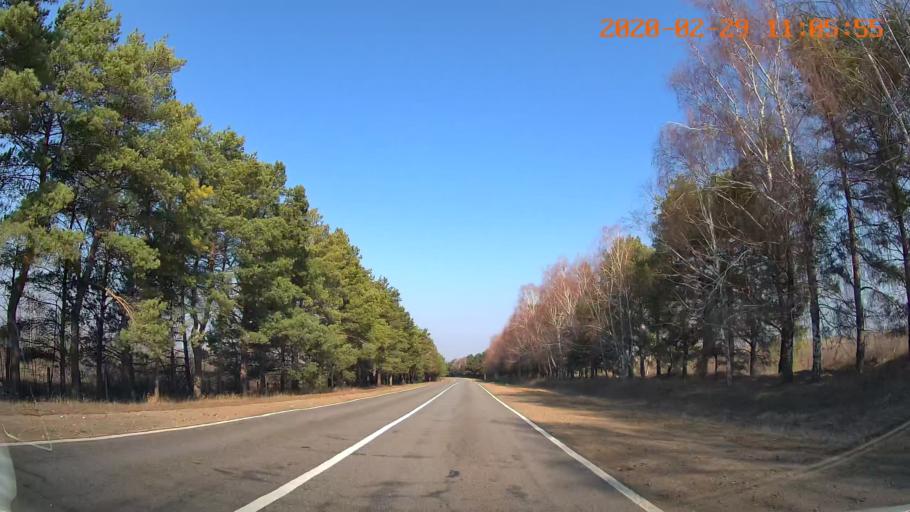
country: MD
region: Criuleni
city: Criuleni
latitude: 47.2080
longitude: 29.1900
